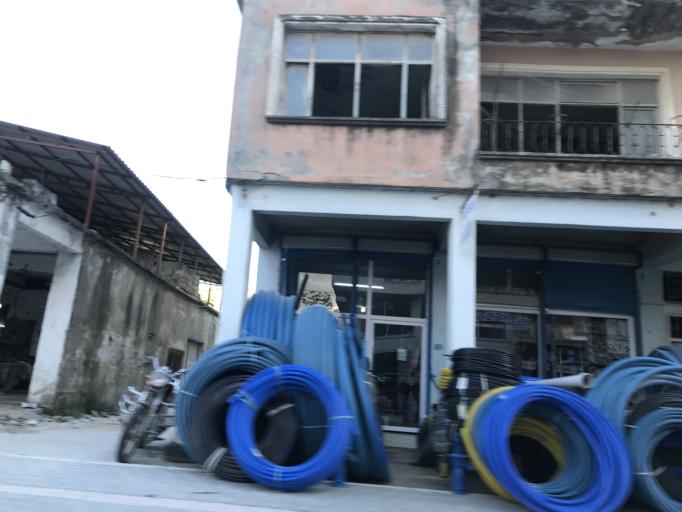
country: TR
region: Hatay
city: Samandag
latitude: 36.0806
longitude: 35.9933
